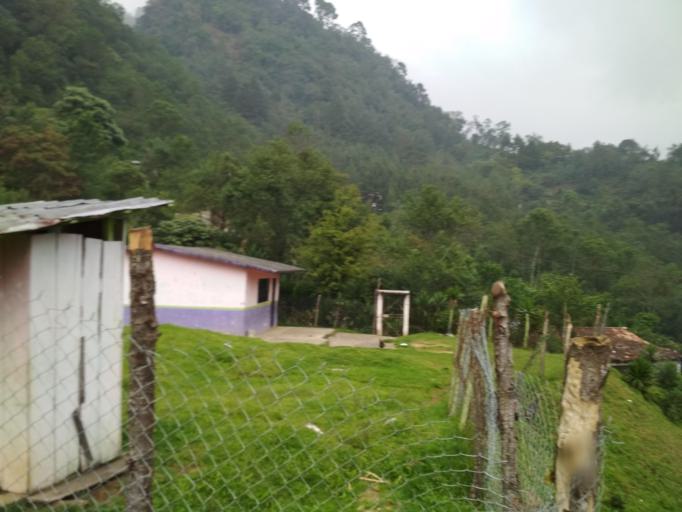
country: MX
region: Veracruz
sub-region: La Perla
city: Metlac Hernandez (Metlac Primero)
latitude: 18.9651
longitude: -97.1287
